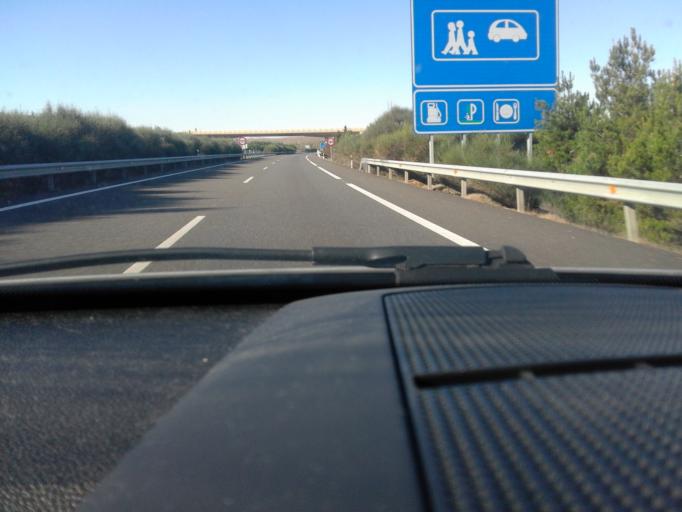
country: ES
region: Castille and Leon
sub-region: Provincia de Leon
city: Campo de Villavidel
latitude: 42.4523
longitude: -5.5077
